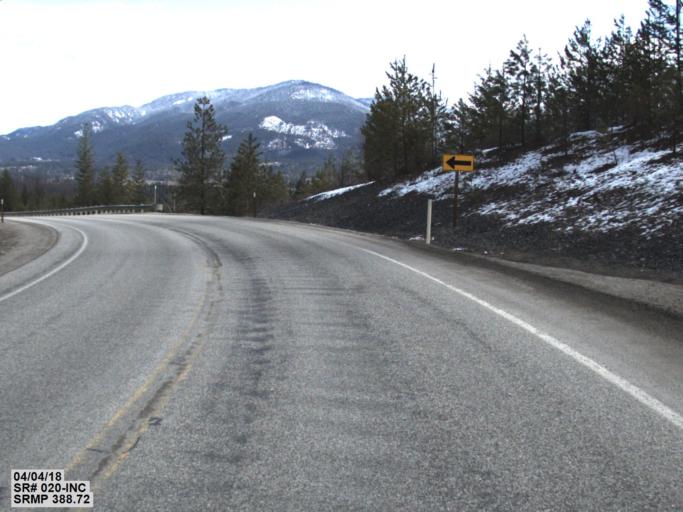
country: CA
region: British Columbia
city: Fruitvale
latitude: 48.6814
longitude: -117.4293
